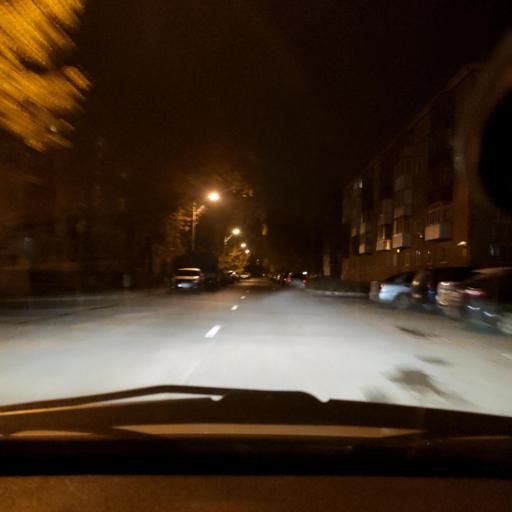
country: RU
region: Bashkortostan
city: Ufa
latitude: 54.8140
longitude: 56.0937
